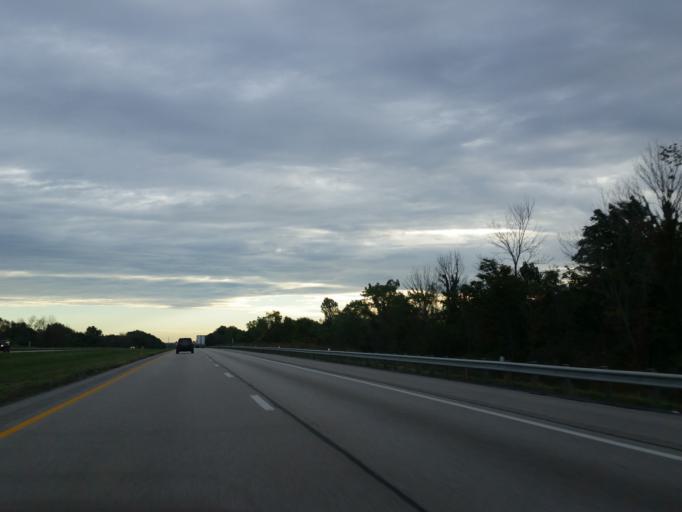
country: US
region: Ohio
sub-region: Ashtabula County
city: North Kingsville
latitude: 41.9004
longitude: -80.6202
